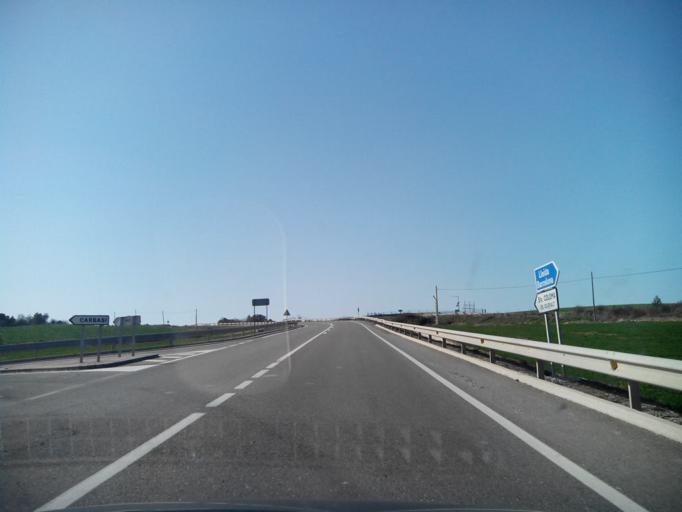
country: ES
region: Catalonia
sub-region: Provincia de Lleida
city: Sant Guim de Freixenet
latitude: 41.6141
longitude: 1.4010
